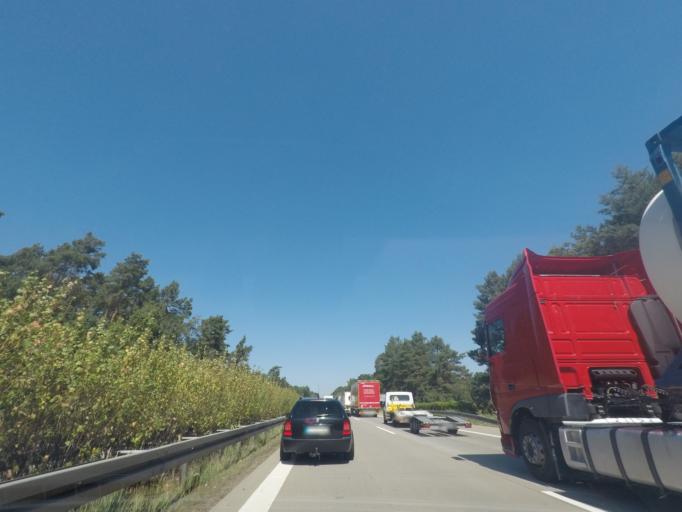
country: DE
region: Brandenburg
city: Bestensee
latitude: 52.2288
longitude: 13.5946
